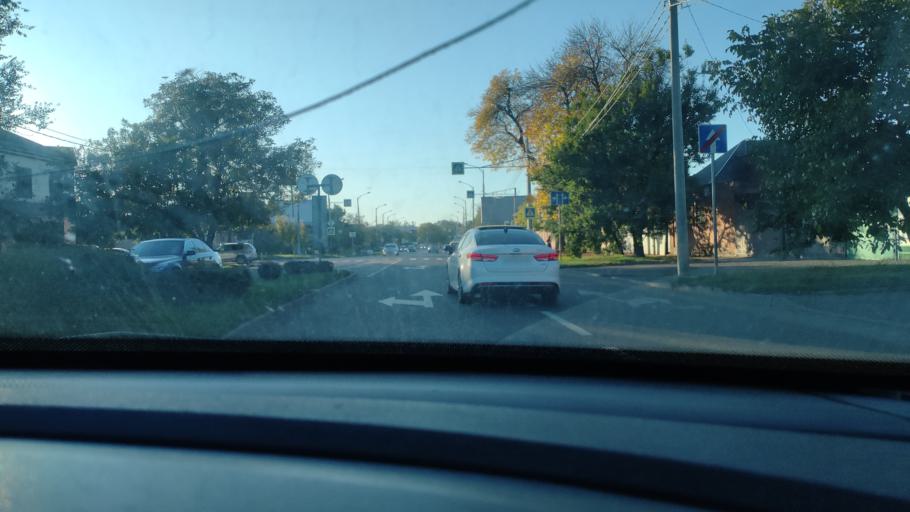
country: RU
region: Krasnodarskiy
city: Krasnodar
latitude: 45.0434
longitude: 38.9355
